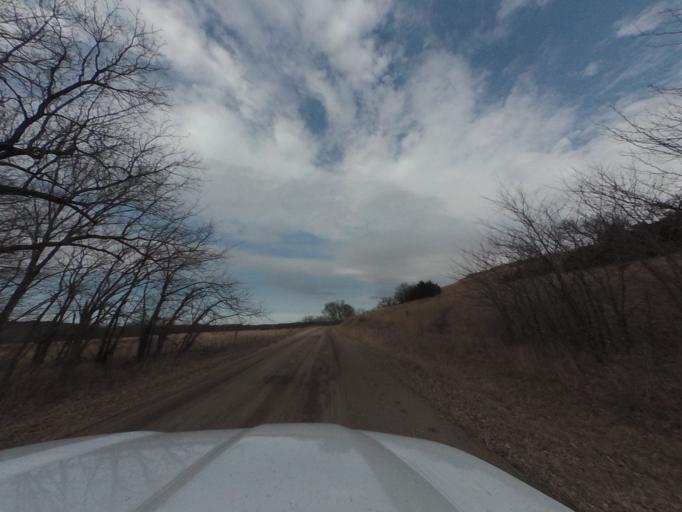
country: US
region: Kansas
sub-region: Chase County
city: Cottonwood Falls
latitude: 38.2791
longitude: -96.7341
